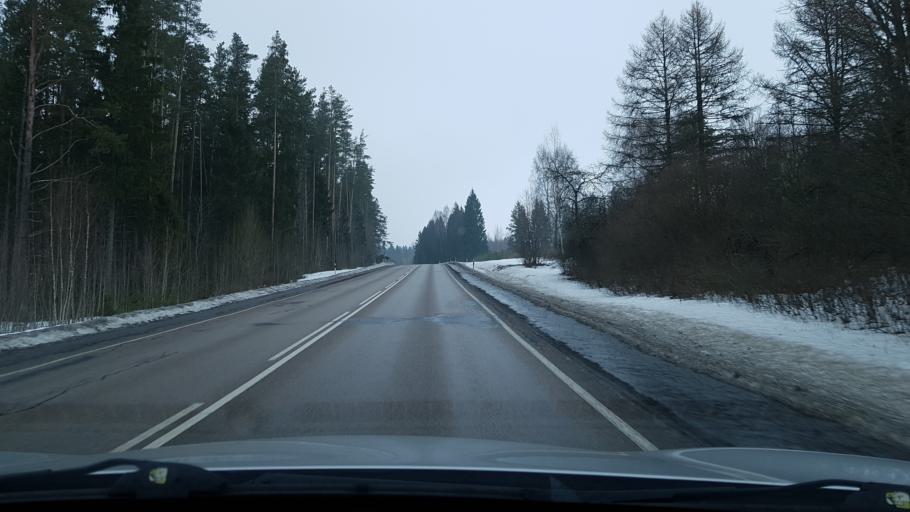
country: EE
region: Valgamaa
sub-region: Torva linn
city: Torva
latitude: 57.9851
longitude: 26.1741
